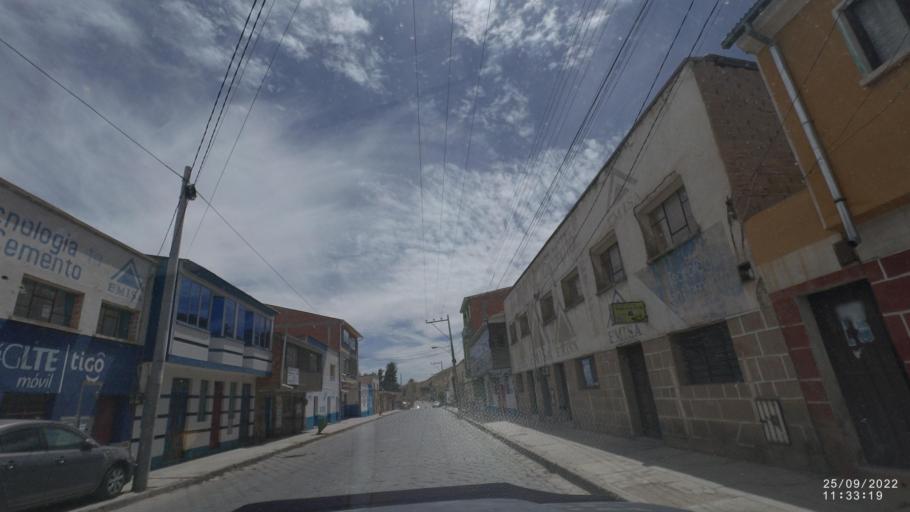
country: BO
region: Oruro
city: Challapata
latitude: -19.0114
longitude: -66.7764
